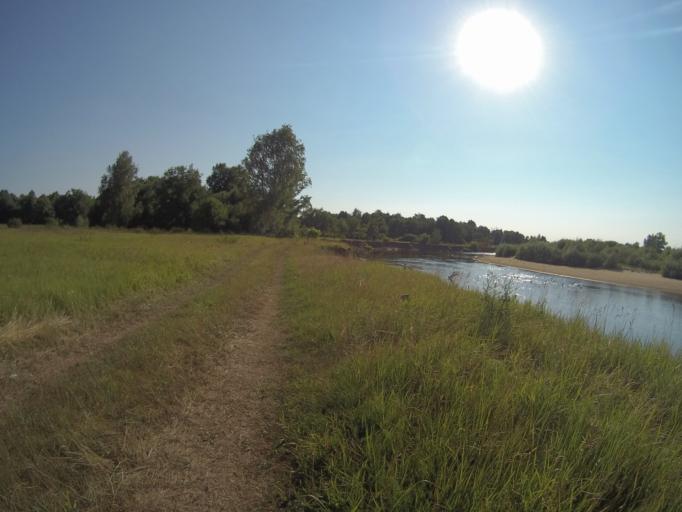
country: RU
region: Vladimir
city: Vorsha
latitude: 56.0343
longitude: 40.2004
